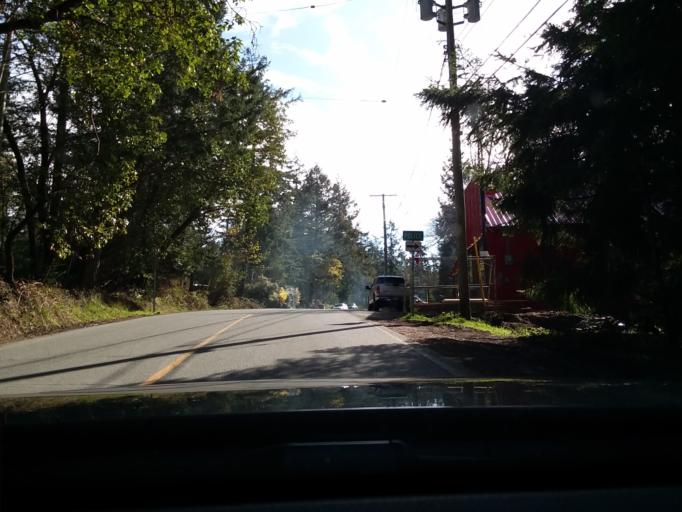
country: CA
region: British Columbia
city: North Saanich
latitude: 48.8793
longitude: -123.3208
